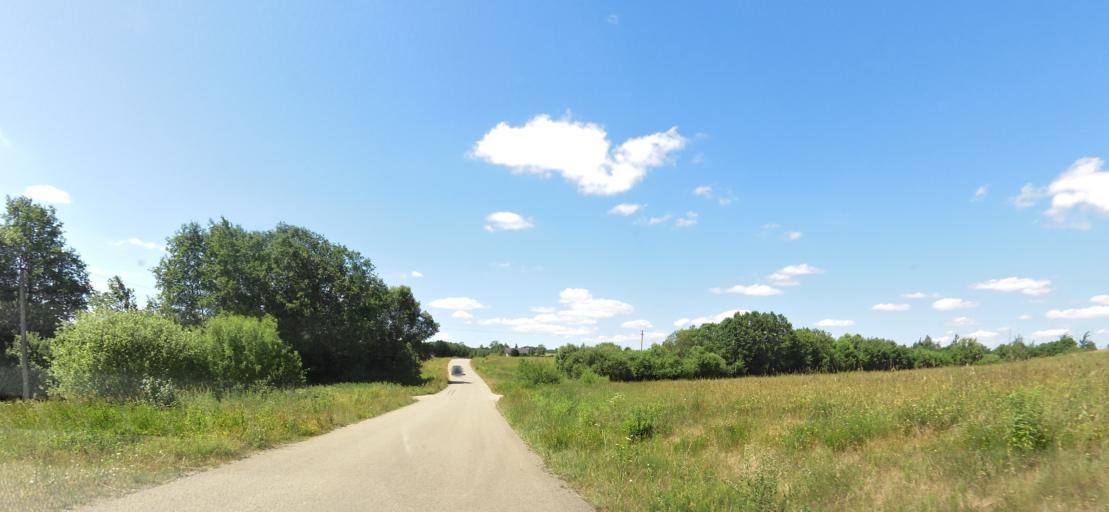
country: LT
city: Nemencine
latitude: 54.8762
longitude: 25.5380
